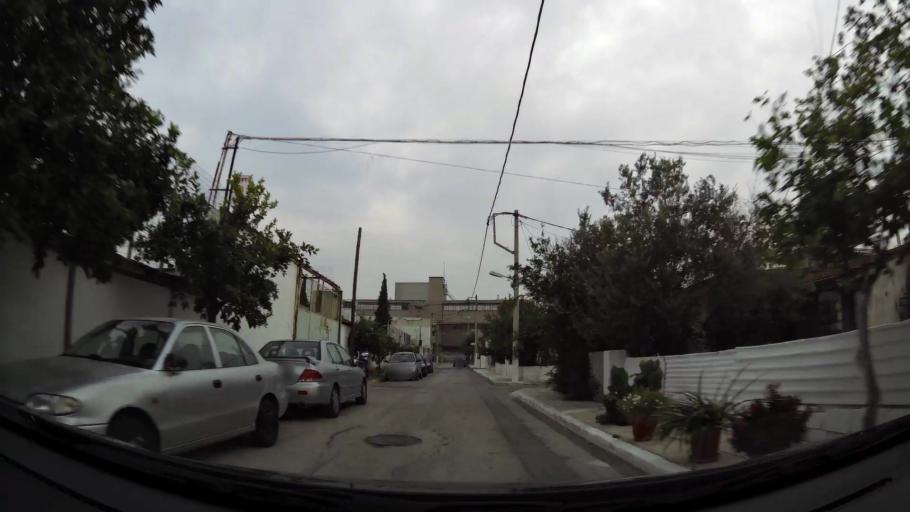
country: GR
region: Attica
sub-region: Nomos Piraios
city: Agios Ioannis Rentis
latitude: 37.9687
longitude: 23.6646
